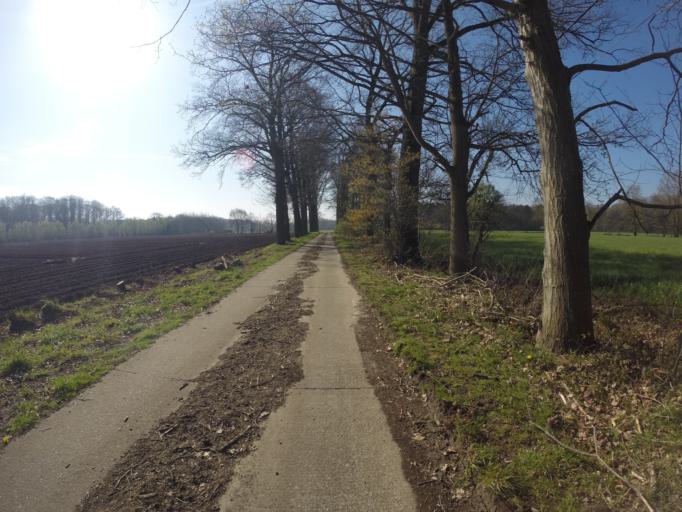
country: BE
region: Flanders
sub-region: Provincie West-Vlaanderen
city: Beernem
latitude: 51.1082
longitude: 3.3637
